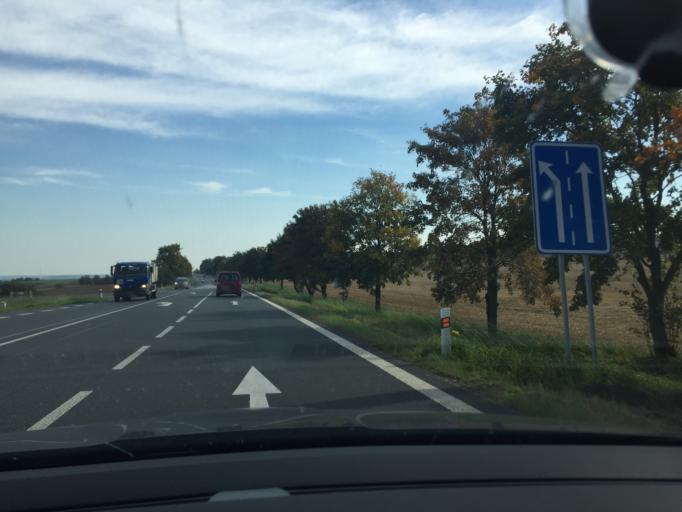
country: CZ
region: Central Bohemia
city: Velim
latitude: 50.0380
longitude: 15.1203
